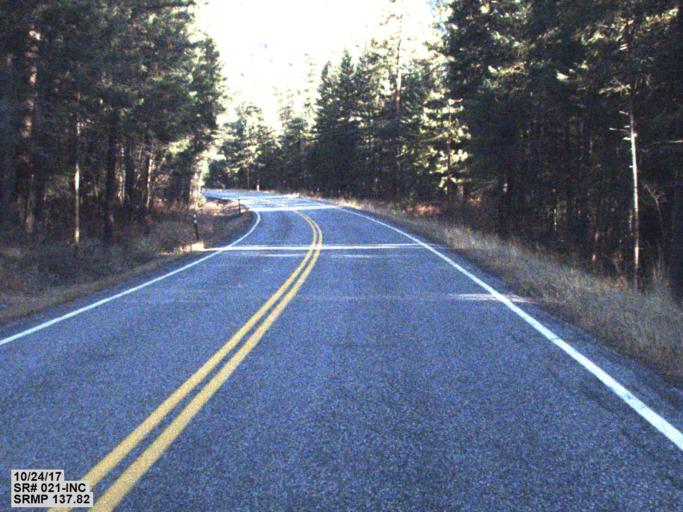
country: US
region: Washington
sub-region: Ferry County
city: Republic
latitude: 48.3598
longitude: -118.7408
